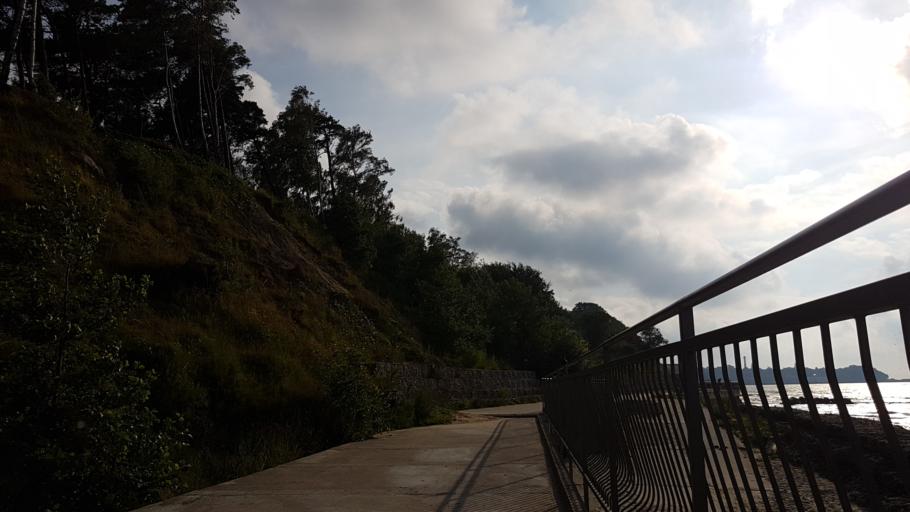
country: RU
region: Kaliningrad
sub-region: Gorod Kaliningrad
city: Pionerskiy
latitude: 54.9556
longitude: 20.2367
